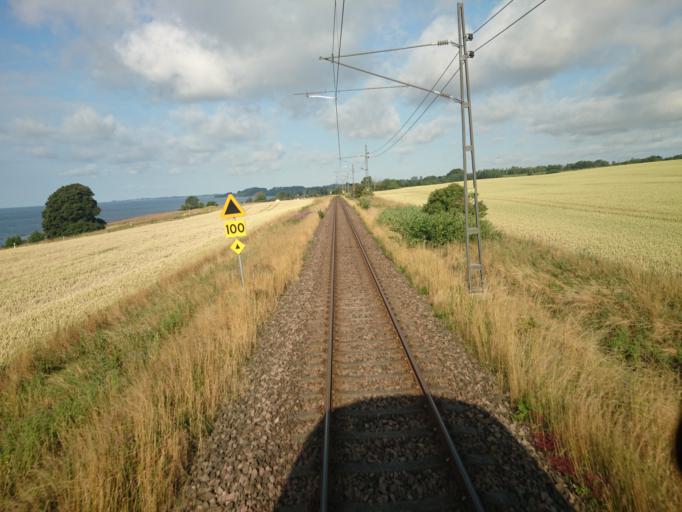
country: SE
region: Skane
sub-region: Ystads Kommun
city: Ystad
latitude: 55.4272
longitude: 13.7381
